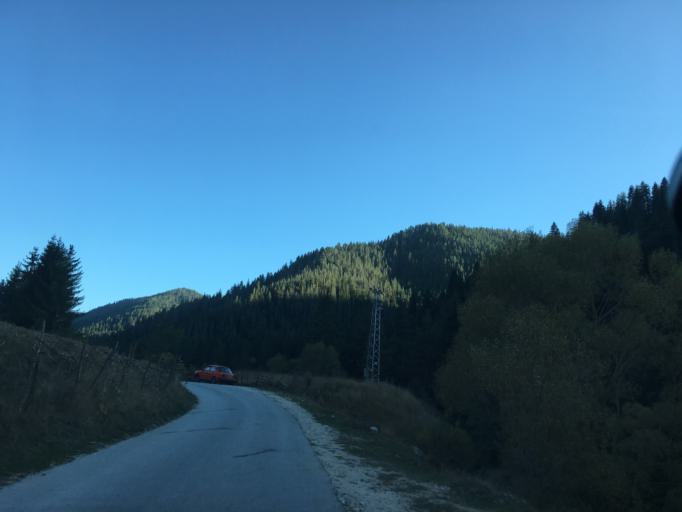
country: BG
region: Smolyan
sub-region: Obshtina Borino
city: Borino
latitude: 41.5900
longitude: 24.3835
